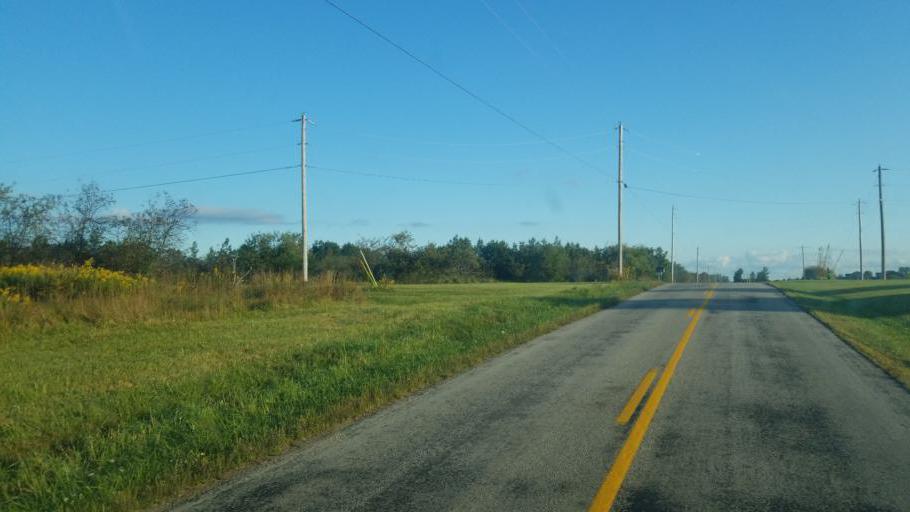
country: US
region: Ohio
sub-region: Lorain County
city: Wellington
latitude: 41.0530
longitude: -82.2589
